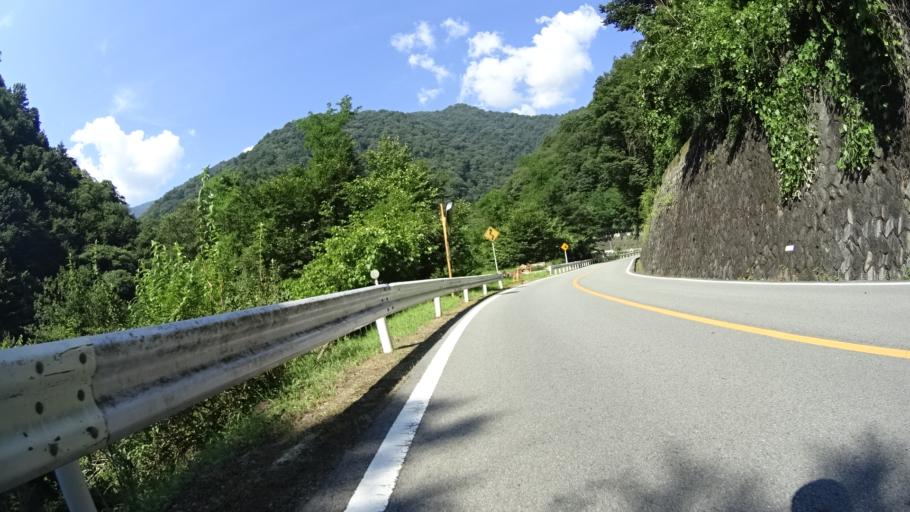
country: JP
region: Yamanashi
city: Enzan
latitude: 35.7957
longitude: 138.8706
